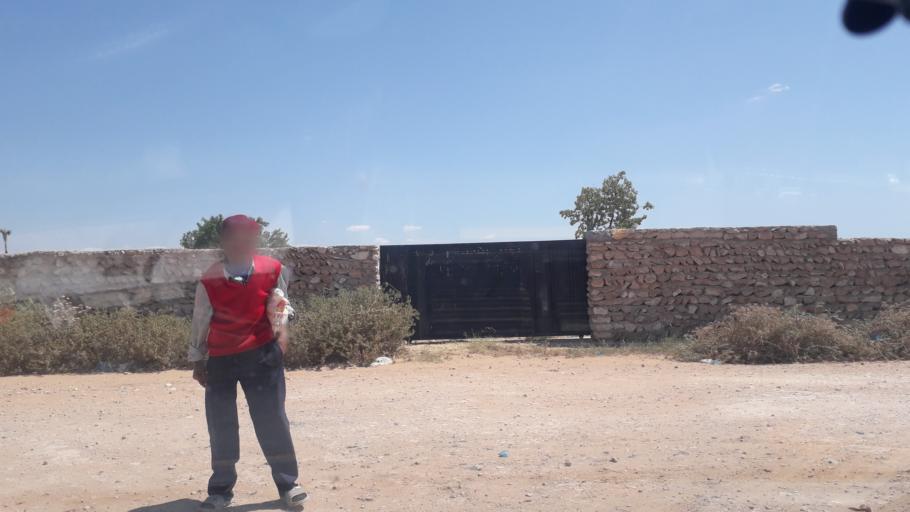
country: TN
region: Safaqis
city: Al Qarmadah
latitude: 34.8367
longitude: 10.7758
